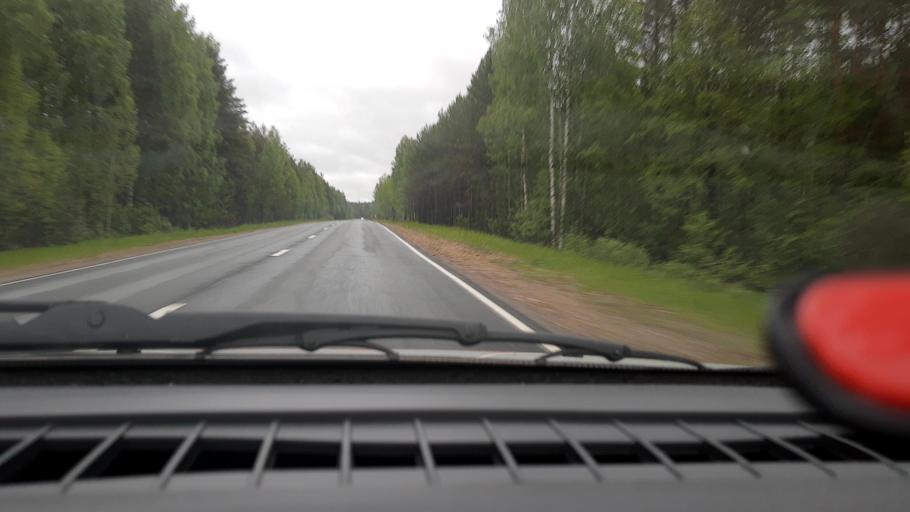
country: RU
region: Nizjnij Novgorod
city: Krasnyye Baki
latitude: 57.1694
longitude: 45.3152
